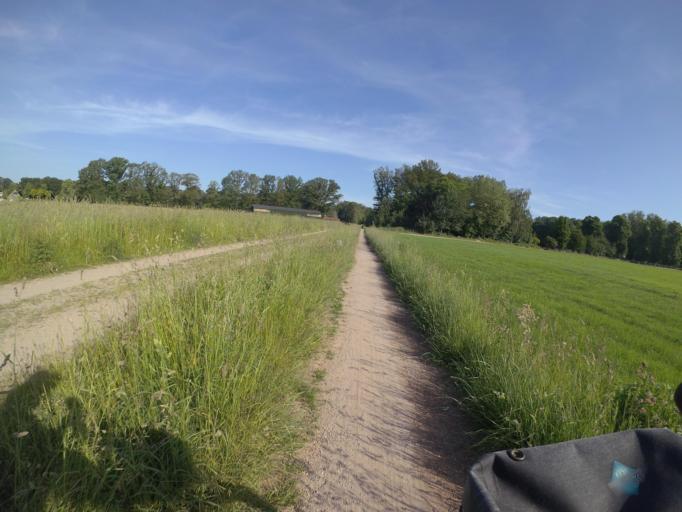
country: NL
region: Gelderland
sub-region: Gemeente Winterswijk
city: Winterswijk
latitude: 51.9849
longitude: 6.7299
